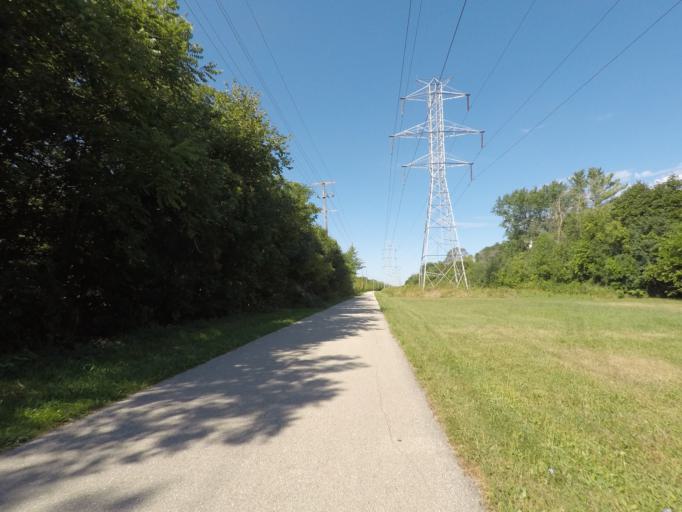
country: US
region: Wisconsin
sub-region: Waukesha County
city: New Berlin
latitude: 43.0102
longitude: -88.1295
